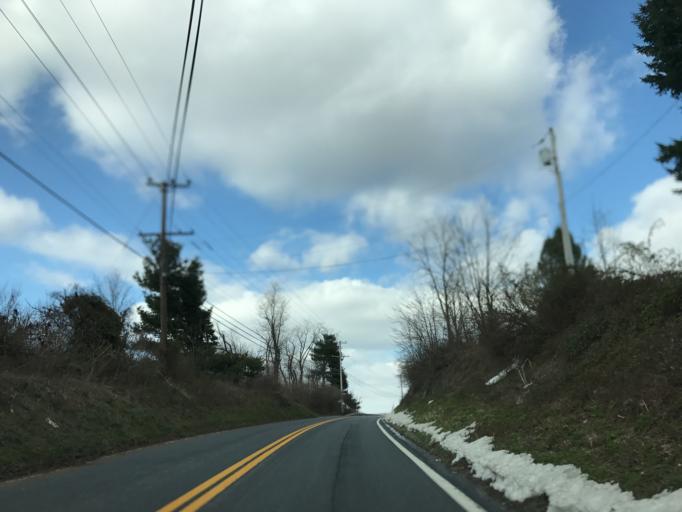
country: US
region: Maryland
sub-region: Carroll County
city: Manchester
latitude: 39.6632
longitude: -76.9467
